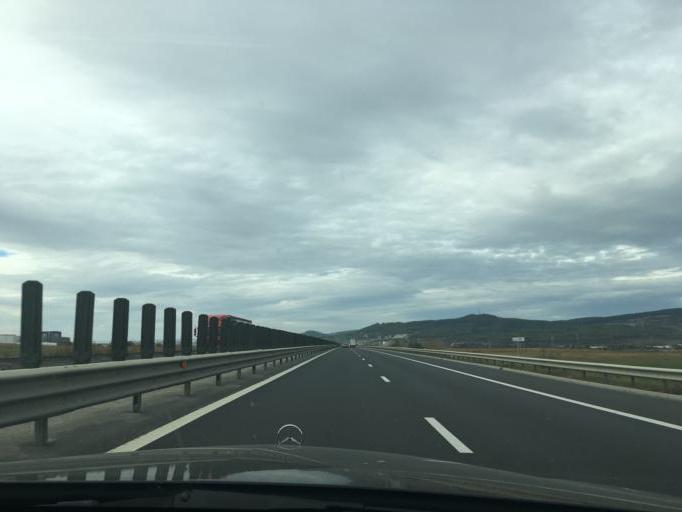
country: RO
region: Sibiu
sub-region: Comuna Selimbar
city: Selimbar
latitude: 45.7738
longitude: 24.2042
